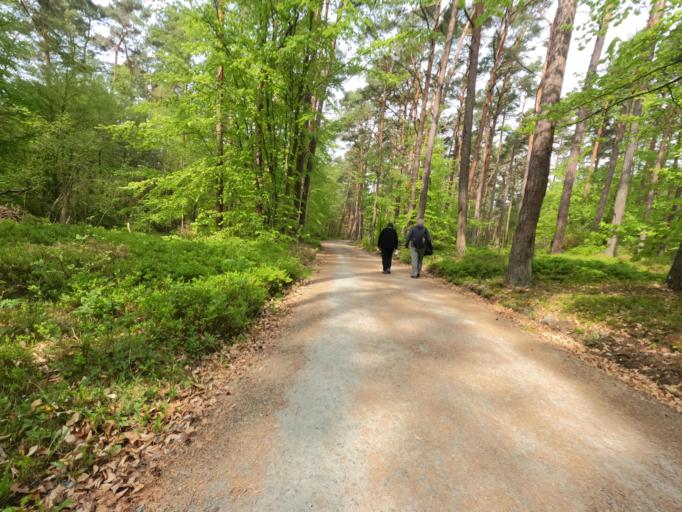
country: DE
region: Mecklenburg-Vorpommern
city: Ostseebad Prerow
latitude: 54.4506
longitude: 12.5213
